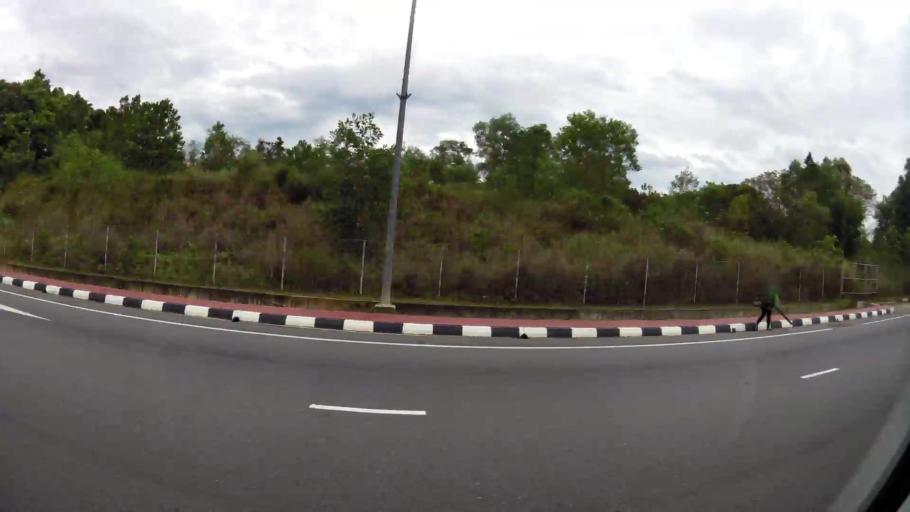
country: BN
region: Brunei and Muara
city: Bandar Seri Begawan
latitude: 4.9185
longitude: 114.9338
